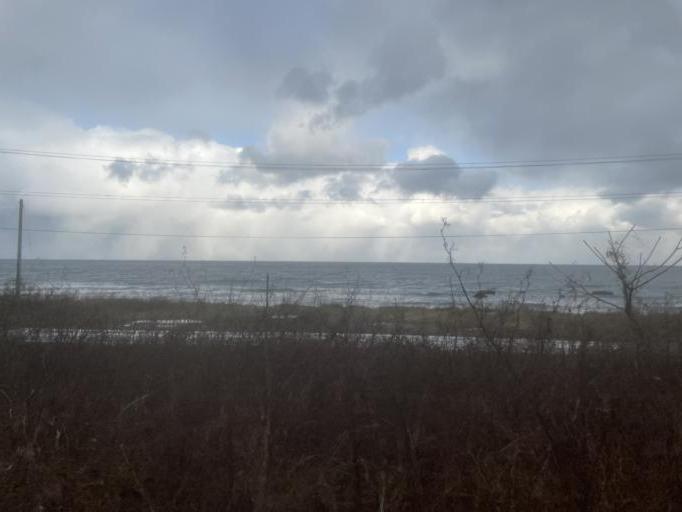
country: JP
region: Aomori
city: Shimokizukuri
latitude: 41.1881
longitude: 140.4552
